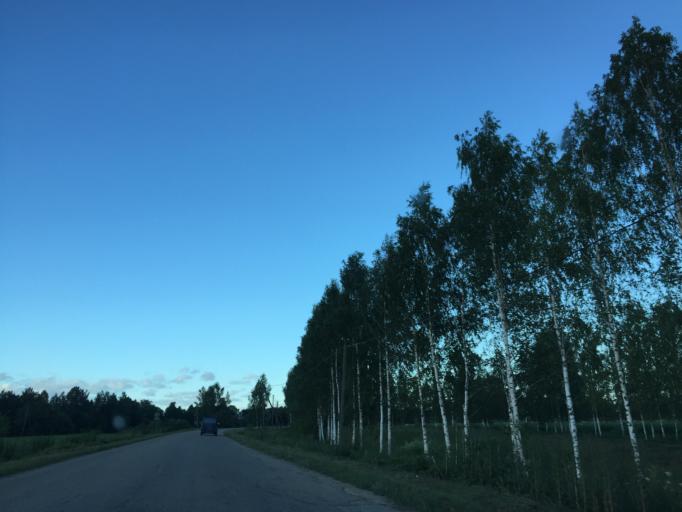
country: LV
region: Plavinu
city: Plavinas
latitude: 56.6087
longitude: 25.8008
